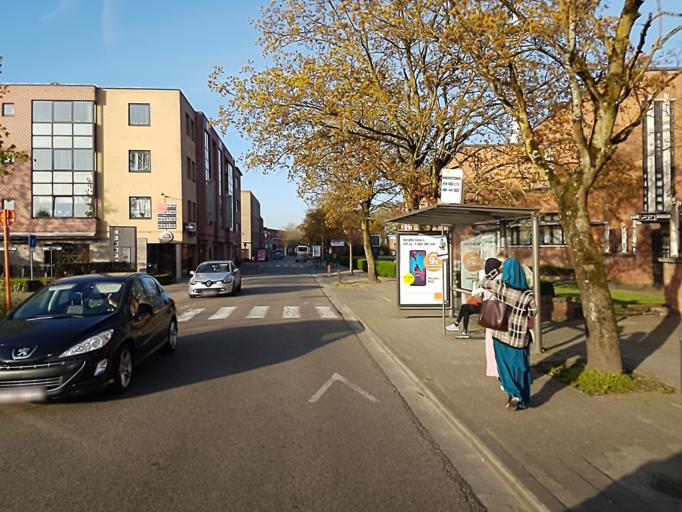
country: BE
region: Flanders
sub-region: Provincie Antwerpen
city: Turnhout
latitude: 51.3159
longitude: 4.9320
